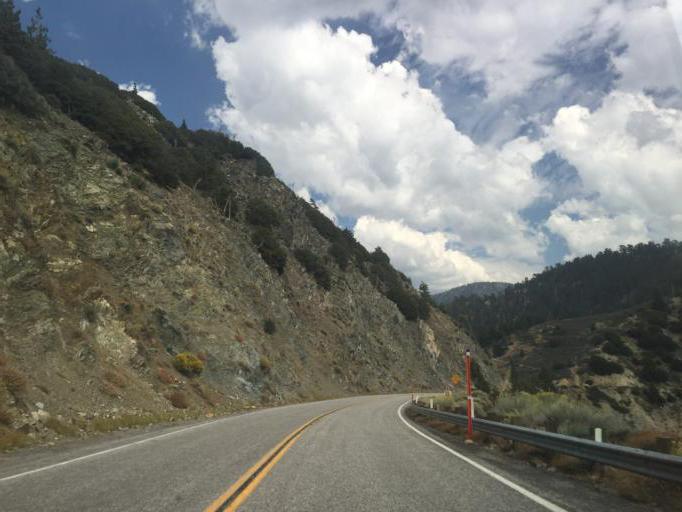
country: US
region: California
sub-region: Los Angeles County
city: Littlerock
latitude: 34.3568
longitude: -117.8558
